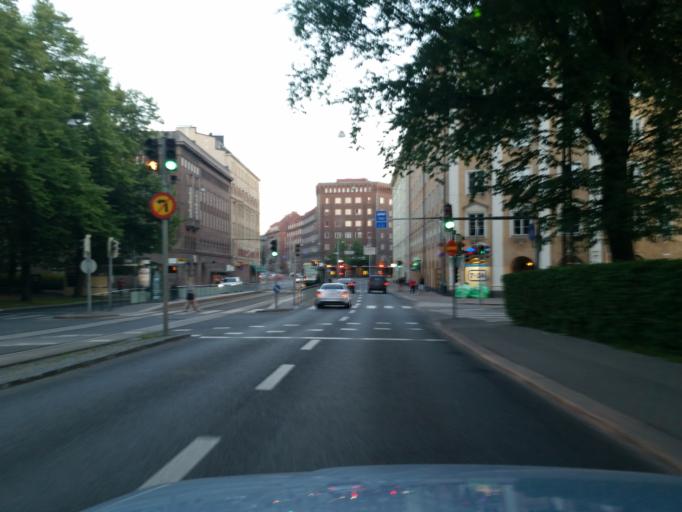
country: FI
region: Uusimaa
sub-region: Helsinki
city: Helsinki
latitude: 60.1768
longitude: 24.9222
